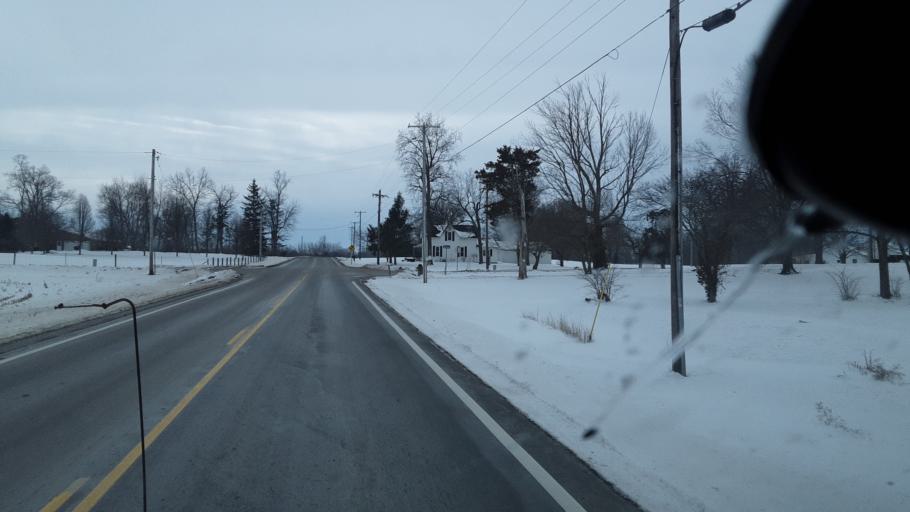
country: US
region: Ohio
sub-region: Madison County
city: London
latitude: 39.8505
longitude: -83.4658
